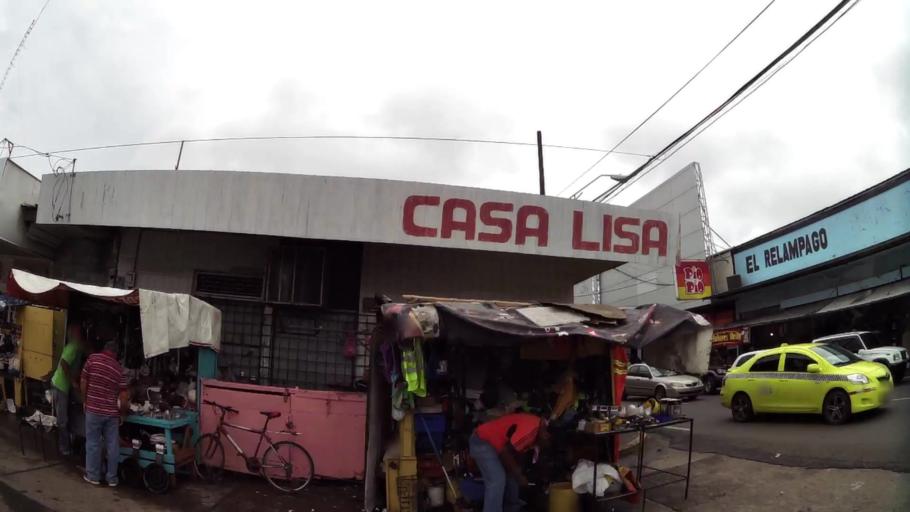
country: PA
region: Chiriqui
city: David
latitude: 8.4309
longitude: -82.4232
